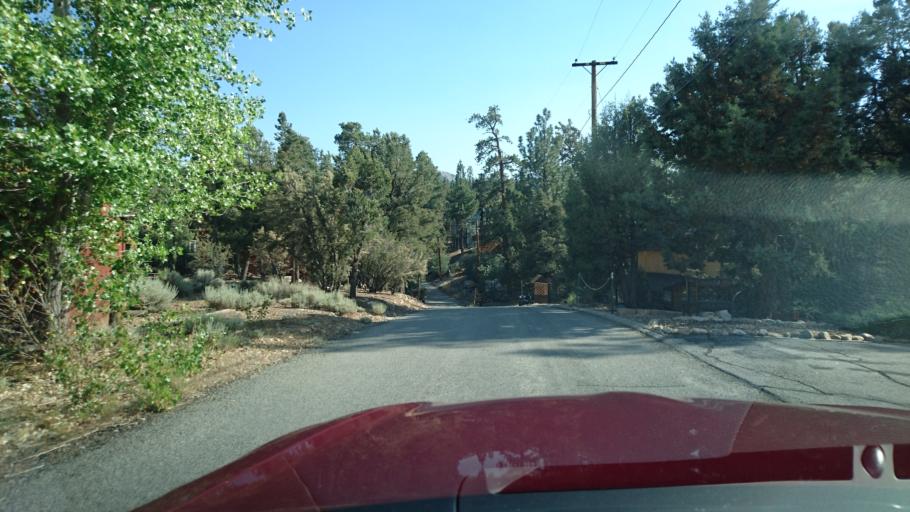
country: US
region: California
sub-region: San Bernardino County
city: Big Bear City
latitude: 34.2494
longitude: -116.8342
